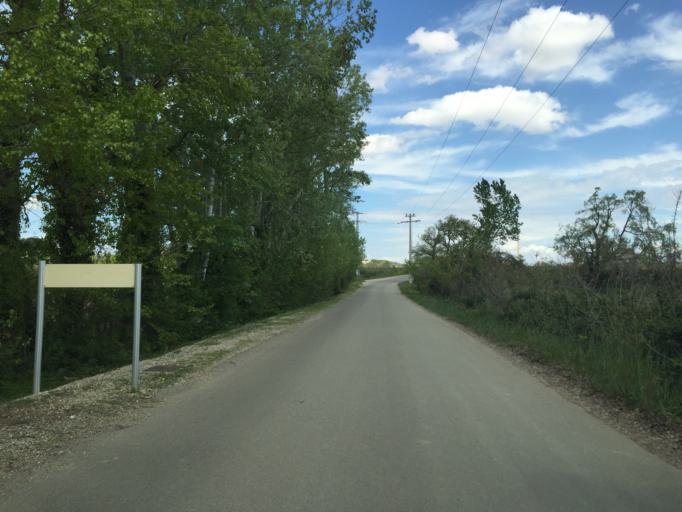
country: FR
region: Provence-Alpes-Cote d'Azur
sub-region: Departement du Vaucluse
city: Chateauneuf-du-Pape
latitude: 44.0424
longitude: 4.8257
